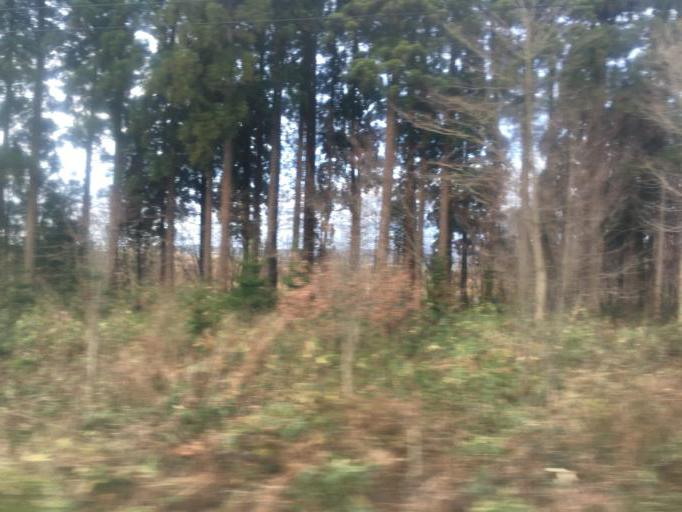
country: JP
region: Akita
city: Takanosu
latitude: 40.2376
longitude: 140.3821
